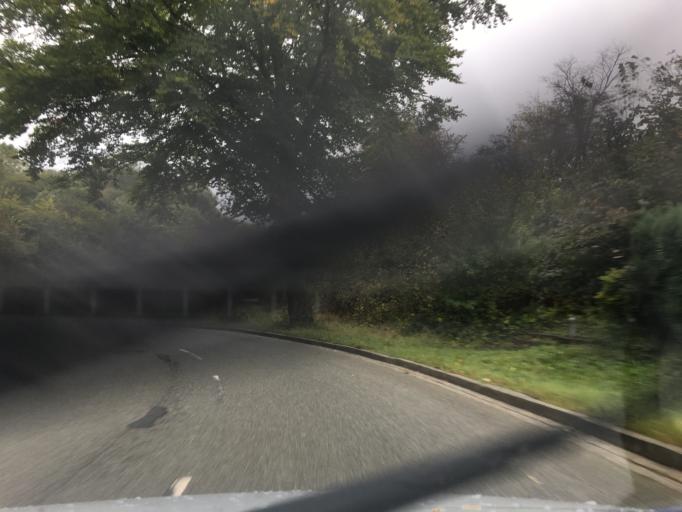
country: DE
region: Schleswig-Holstein
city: Quarnbek
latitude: 54.3449
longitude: 9.9876
